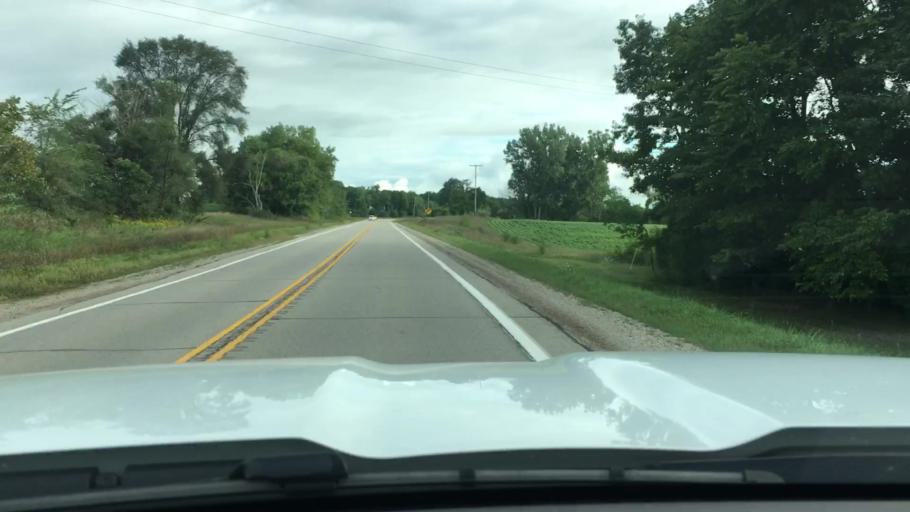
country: US
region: Michigan
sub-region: Tuscola County
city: Caro
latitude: 43.5293
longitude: -83.3455
